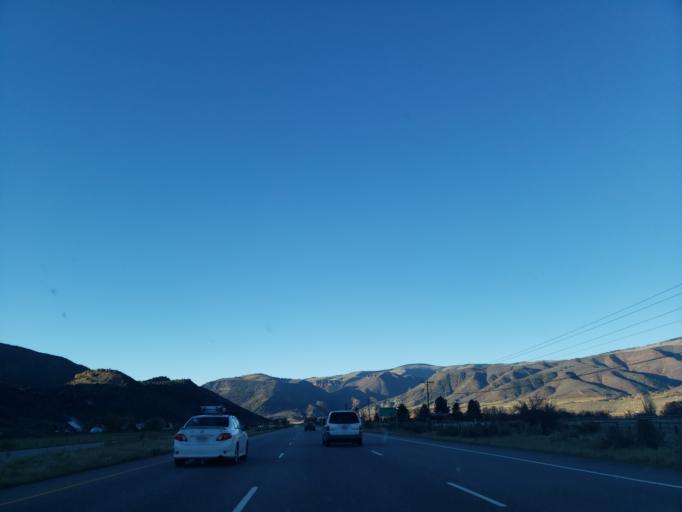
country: US
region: Colorado
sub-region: Pitkin County
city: Snowmass Village
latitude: 39.2520
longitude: -106.8845
